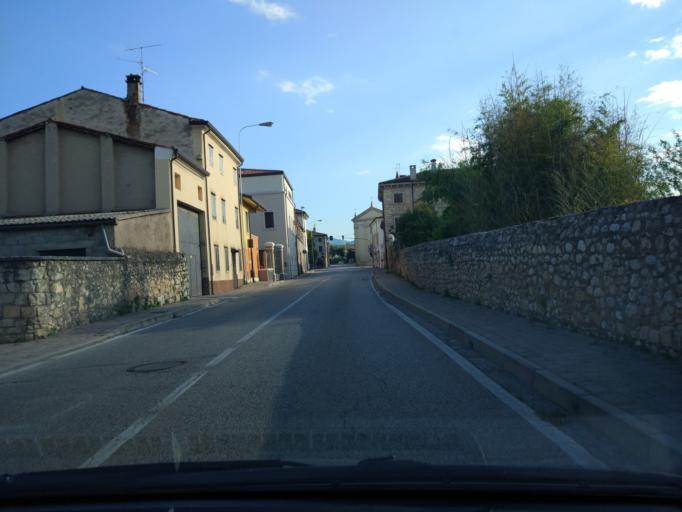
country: IT
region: Veneto
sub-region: Provincia di Verona
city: Colognola ai Colli
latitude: 45.4397
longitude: 11.1784
